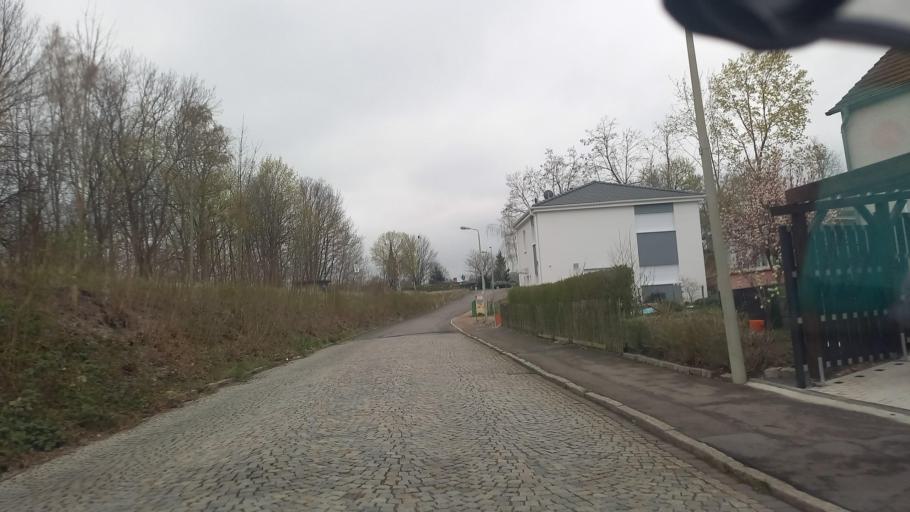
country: DE
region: Saxony
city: Zwickau
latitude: 50.7008
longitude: 12.4955
